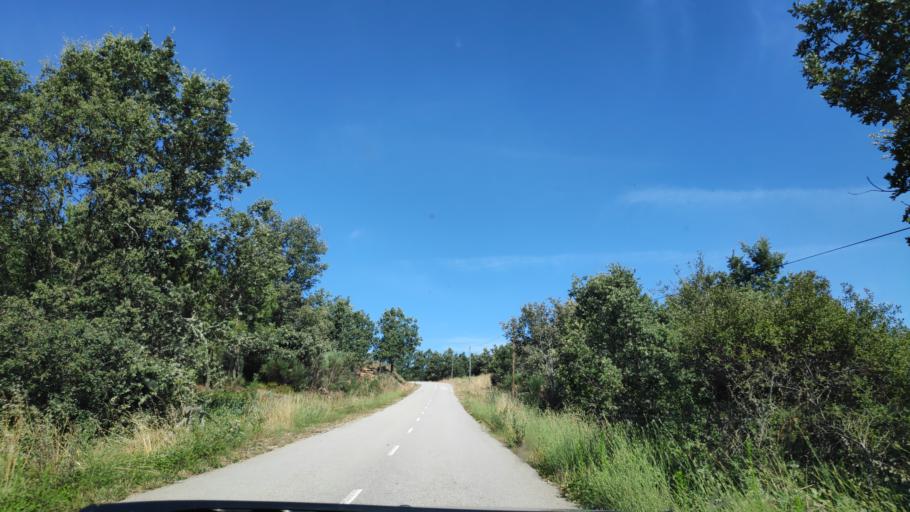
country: ES
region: Castille and Leon
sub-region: Provincia de Zamora
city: Alcanices
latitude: 41.6477
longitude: -6.3654
